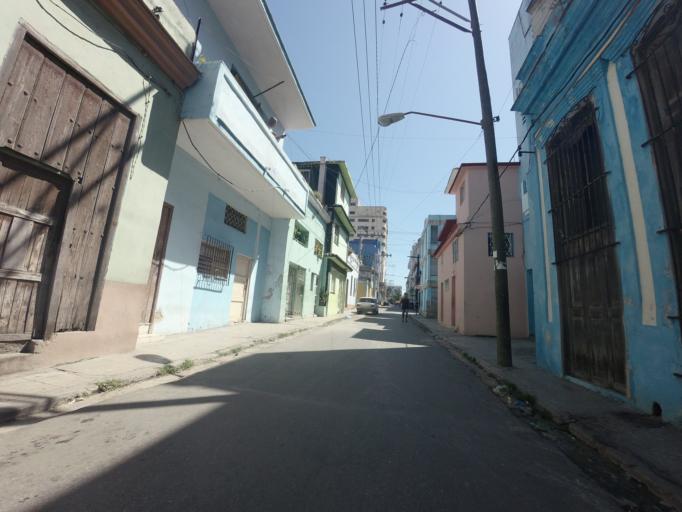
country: CU
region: La Habana
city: Centro Habana
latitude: 23.1334
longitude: -82.3705
